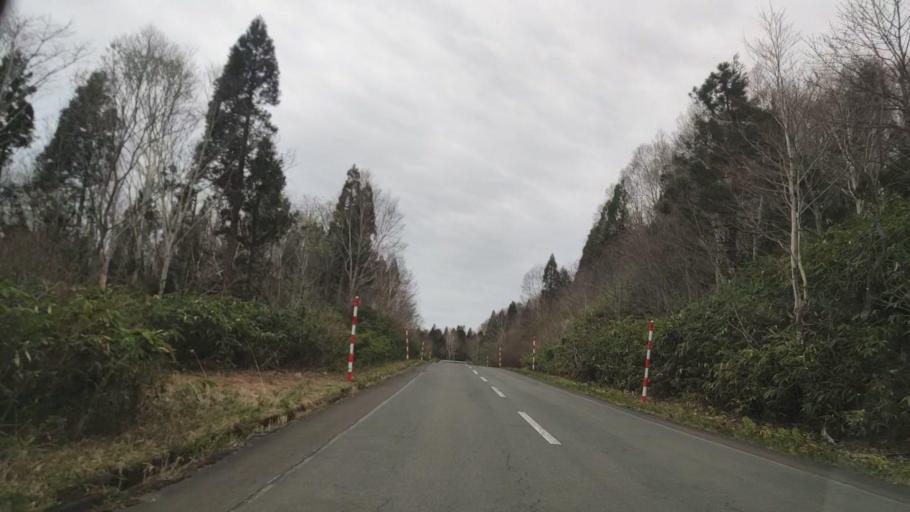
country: JP
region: Akita
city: Hanawa
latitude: 40.4173
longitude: 140.8451
